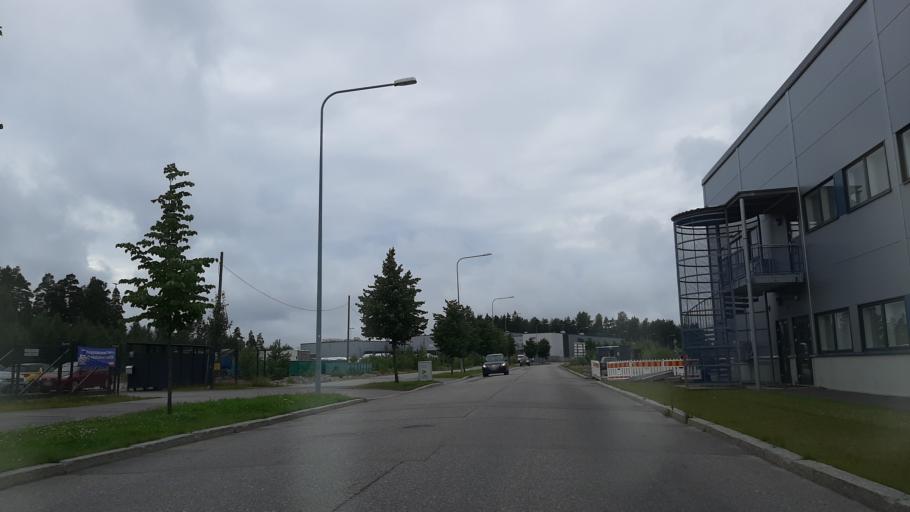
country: FI
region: Uusimaa
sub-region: Helsinki
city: Vantaa
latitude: 60.2442
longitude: 25.0591
